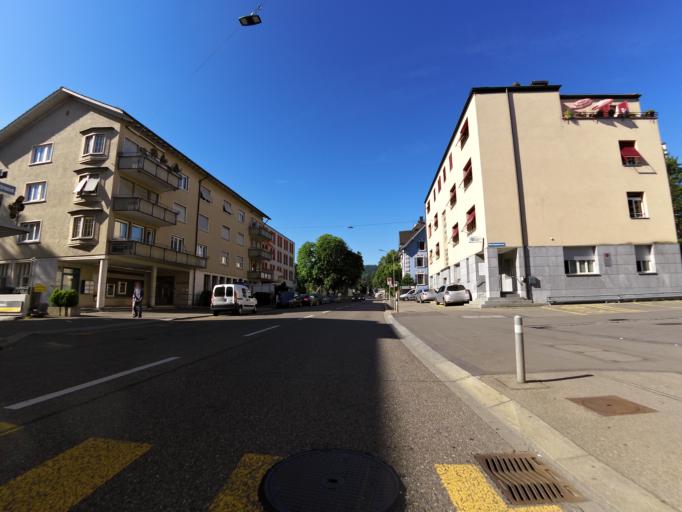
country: CH
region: Zurich
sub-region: Bezirk Zuerich
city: Zuerich (Kreis 9) / Altstetten
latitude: 47.3872
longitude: 8.4863
